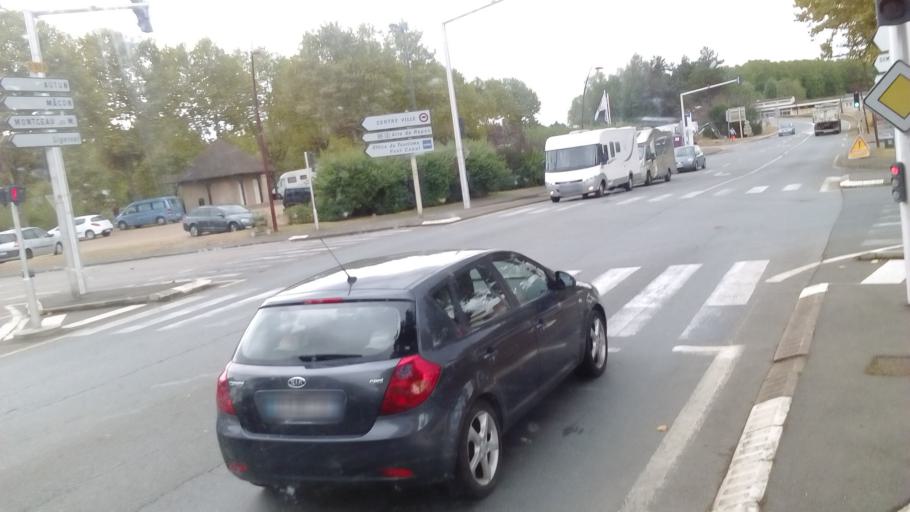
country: FR
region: Bourgogne
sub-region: Departement de Saone-et-Loire
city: Digoin
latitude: 46.4816
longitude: 3.9721
